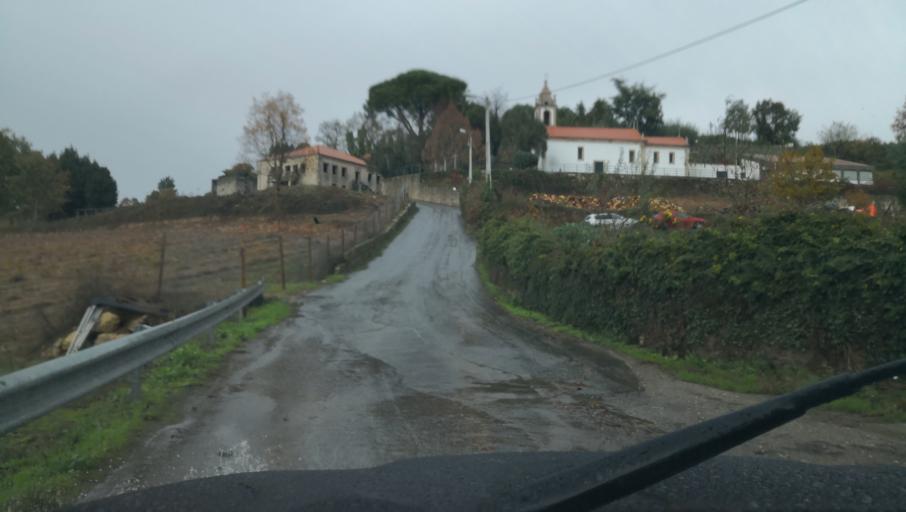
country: PT
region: Vila Real
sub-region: Vila Real
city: Vila Real
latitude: 41.2917
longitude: -7.7105
